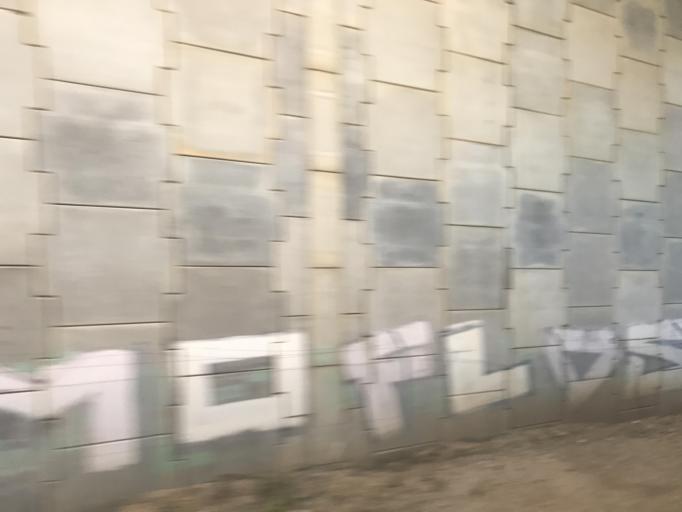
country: ES
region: Castille and Leon
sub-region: Provincia de Valladolid
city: Santovenia de Pisuerga
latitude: 41.7050
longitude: -4.6723
